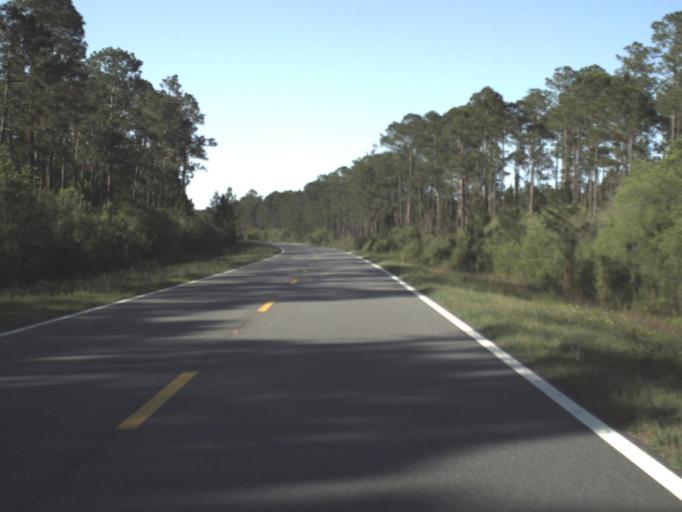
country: US
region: Florida
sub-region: Liberty County
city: Bristol
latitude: 30.2942
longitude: -84.8337
